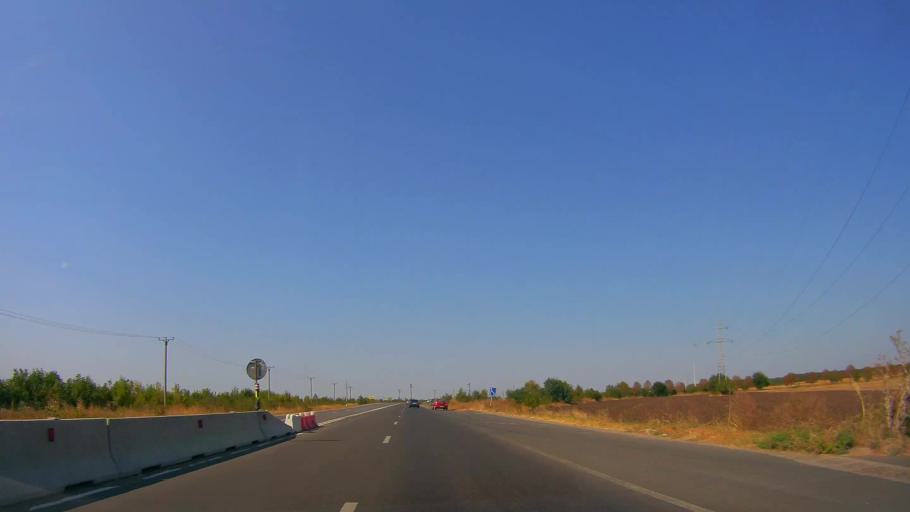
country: RO
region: Giurgiu
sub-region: Comuna Daia
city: Plopsoru
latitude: 44.0196
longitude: 25.9741
